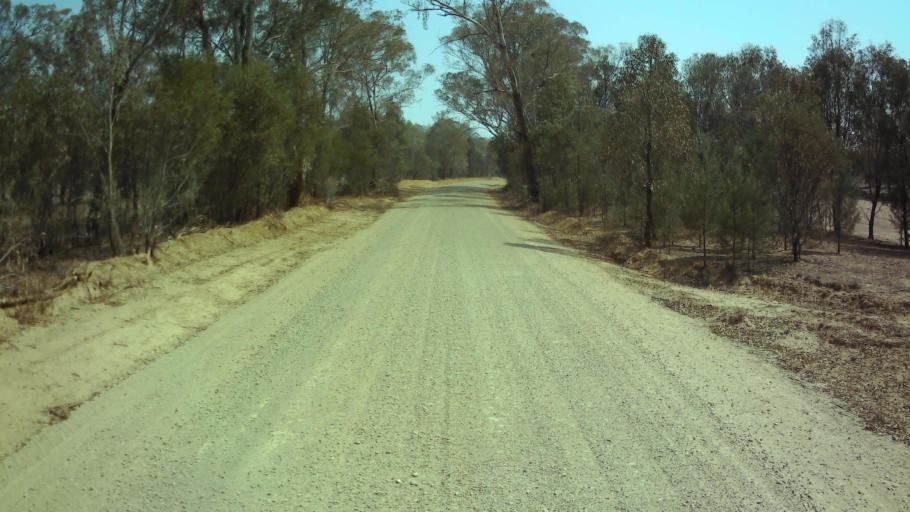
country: AU
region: New South Wales
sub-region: Weddin
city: Grenfell
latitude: -33.6659
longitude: 148.2744
